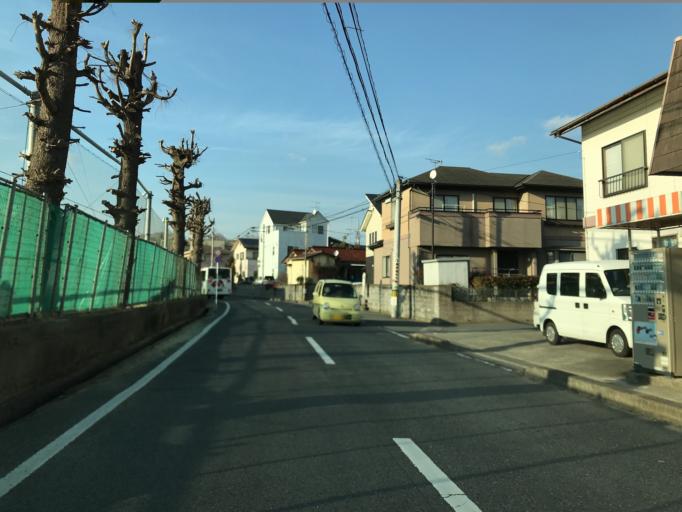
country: JP
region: Fukushima
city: Iwaki
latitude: 37.0424
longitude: 140.8524
